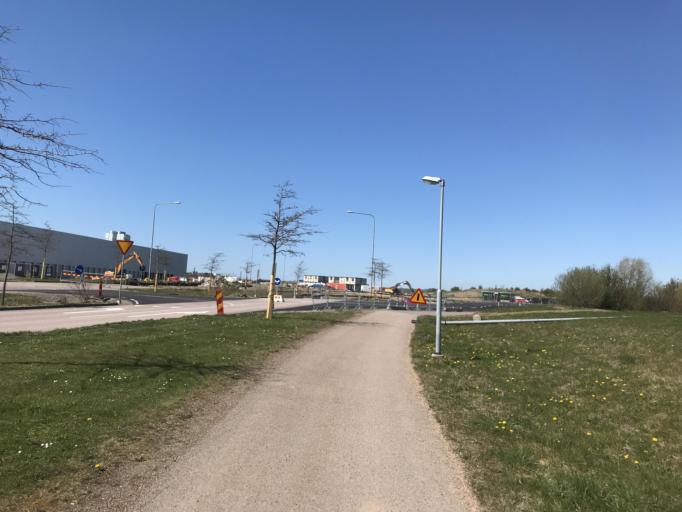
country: SE
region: Skane
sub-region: Landskrona
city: Landskrona
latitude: 55.8754
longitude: 12.8676
